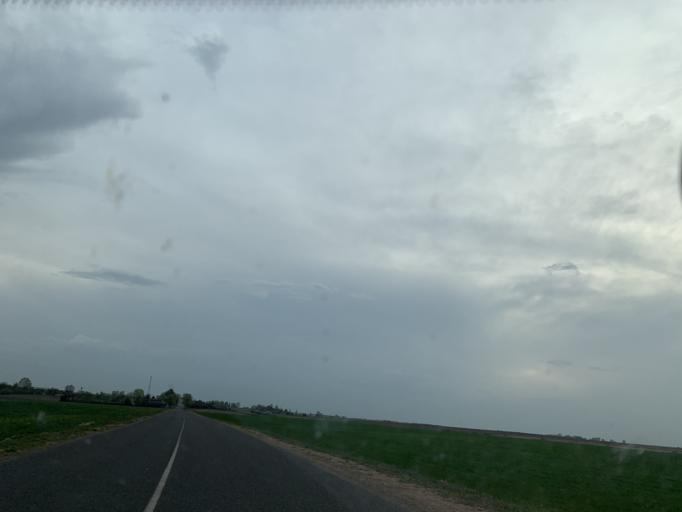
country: BY
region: Minsk
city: Kapyl'
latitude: 53.2890
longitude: 26.9898
